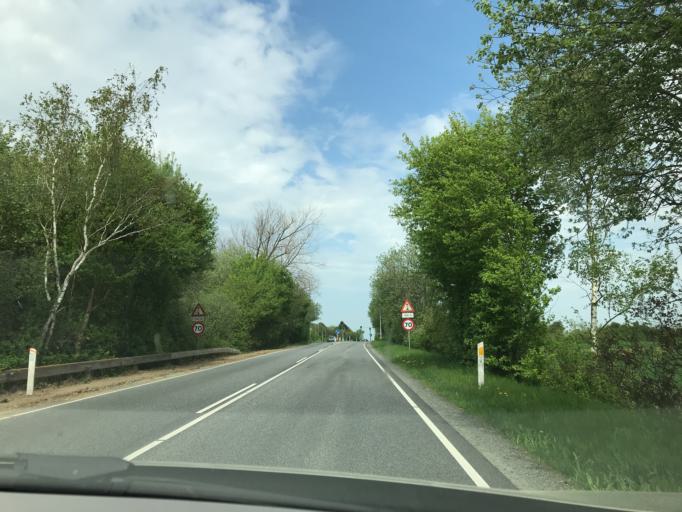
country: DK
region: South Denmark
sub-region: Assens Kommune
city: Assens
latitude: 55.2796
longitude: 9.9206
